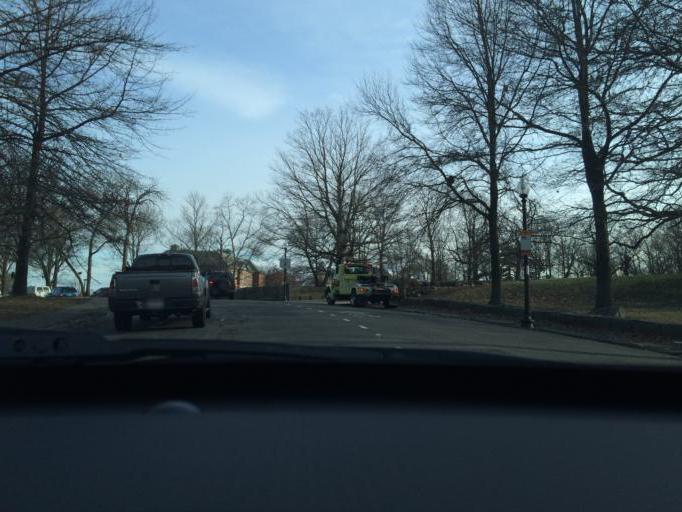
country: US
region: Massachusetts
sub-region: Suffolk County
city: Jamaica Plain
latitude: 42.3021
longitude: -71.0873
